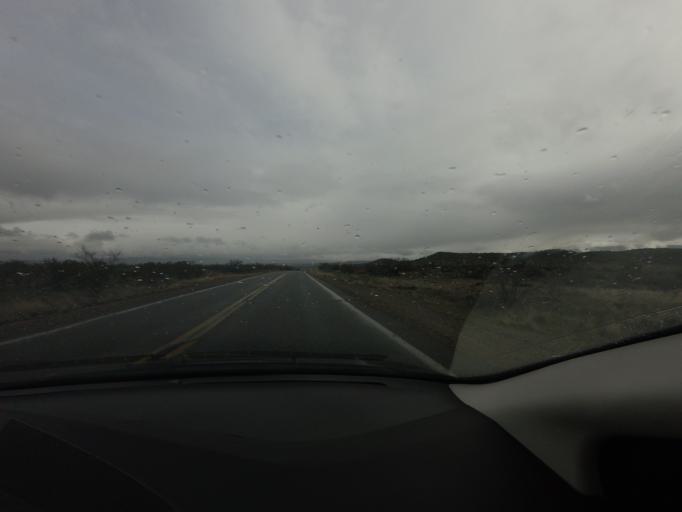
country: US
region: Arizona
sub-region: Yavapai County
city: Lake Montezuma
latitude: 34.6747
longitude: -111.8369
